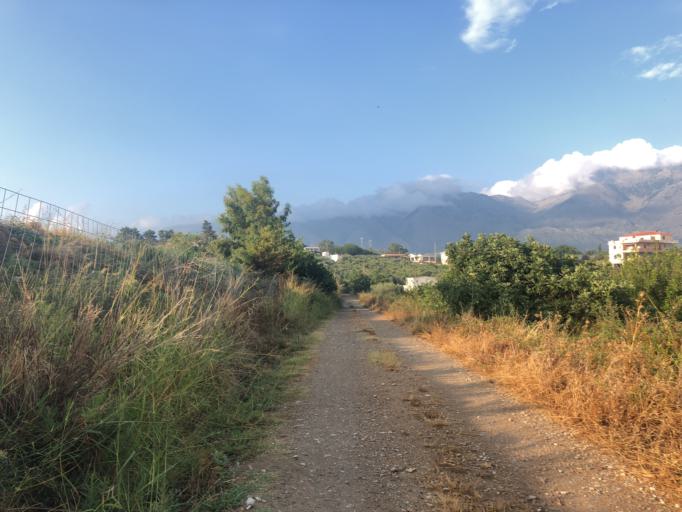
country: GR
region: Crete
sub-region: Nomos Chanias
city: Georgioupolis
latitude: 35.3471
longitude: 24.3138
